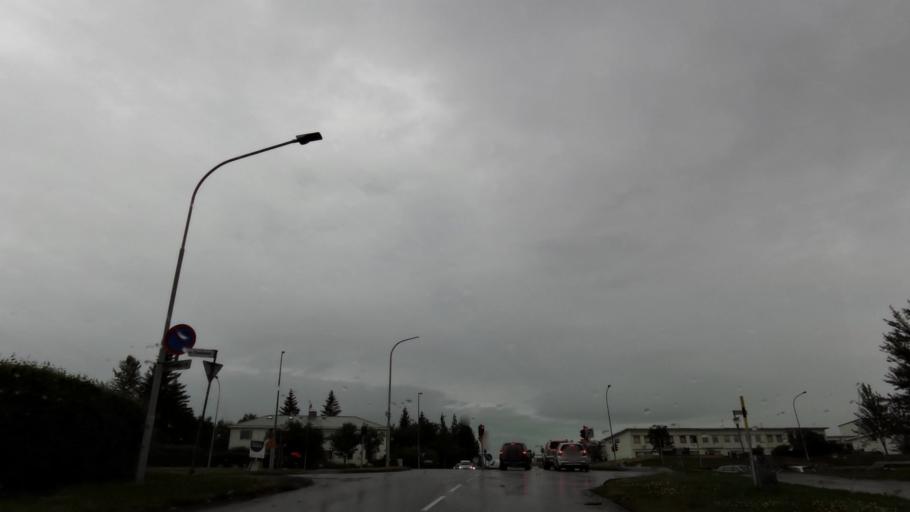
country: IS
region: Capital Region
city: Reykjavik
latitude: 64.1214
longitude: -21.8704
